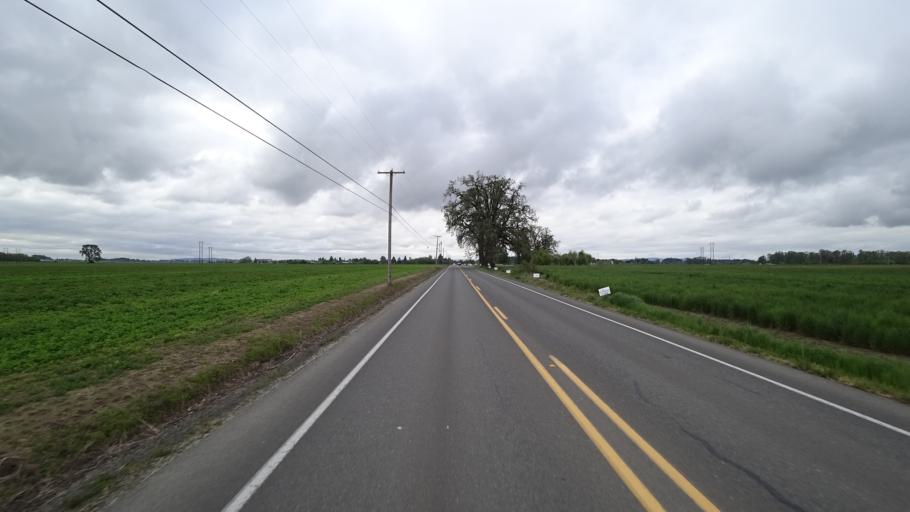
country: US
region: Oregon
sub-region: Washington County
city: Hillsboro
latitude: 45.5601
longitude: -122.9729
